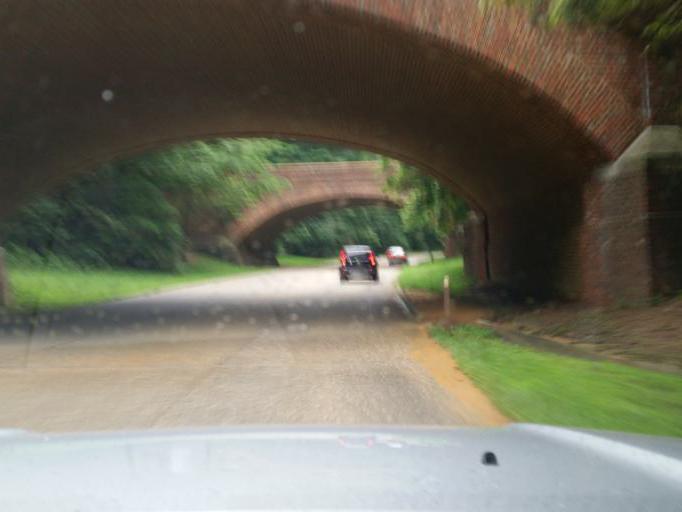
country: US
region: Virginia
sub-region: City of Williamsburg
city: Williamsburg
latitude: 37.2780
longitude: -76.6623
